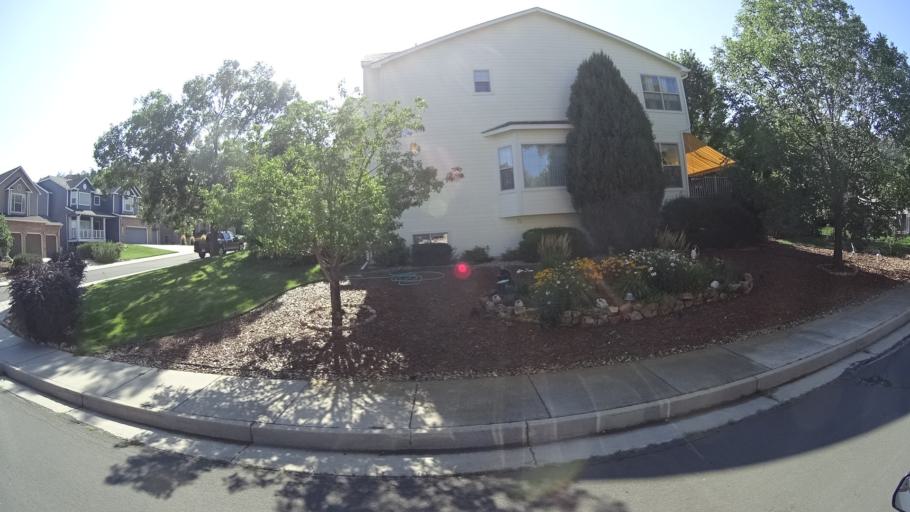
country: US
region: Colorado
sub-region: El Paso County
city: Colorado Springs
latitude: 38.8870
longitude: -104.7837
